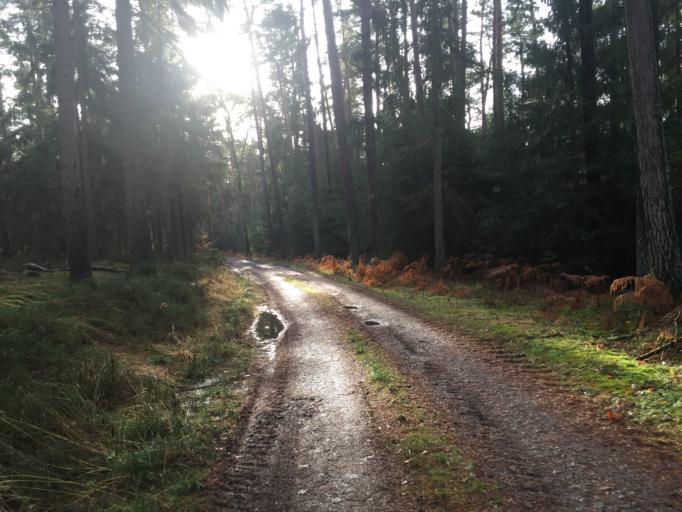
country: DE
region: Hesse
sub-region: Regierungsbezirk Darmstadt
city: Frankisch-Crumbach
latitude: 49.7006
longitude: 8.9198
